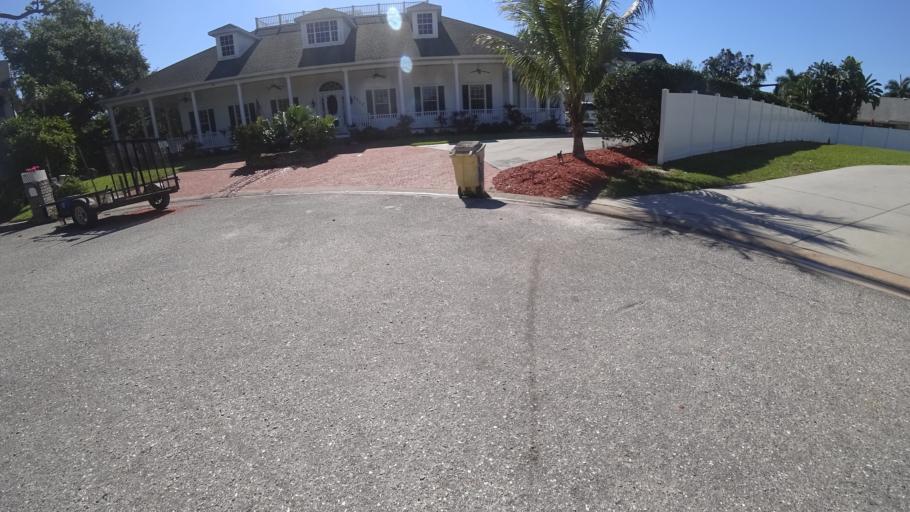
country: US
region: Florida
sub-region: Manatee County
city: West Bradenton
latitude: 27.4842
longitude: -82.6416
